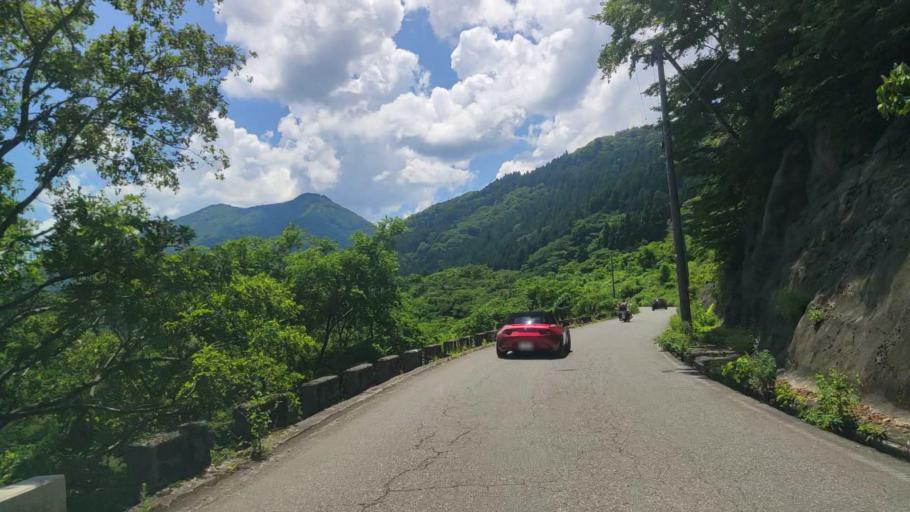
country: JP
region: Fukui
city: Ono
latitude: 35.8880
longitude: 136.5063
